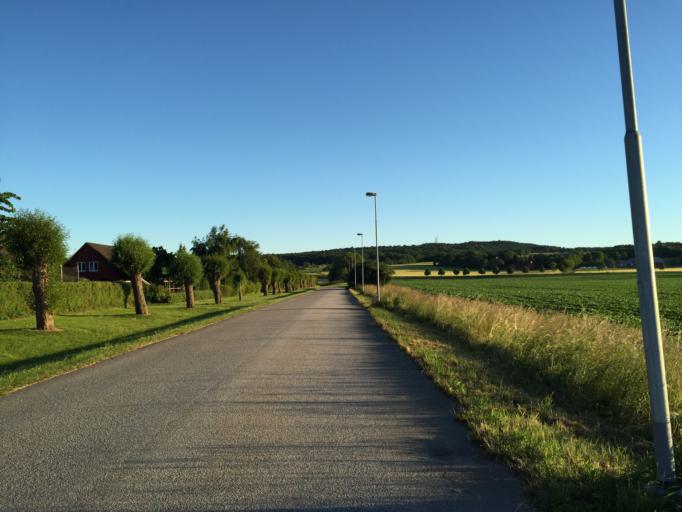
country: SE
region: Skane
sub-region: Lunds Kommun
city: Veberod
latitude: 55.6369
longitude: 13.4806
